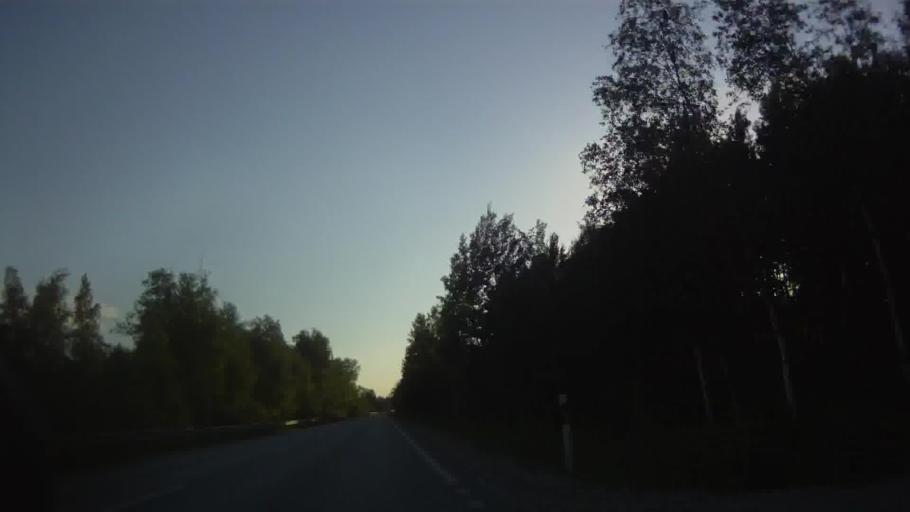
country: LV
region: Livani
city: Livani
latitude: 56.5292
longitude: 26.3819
